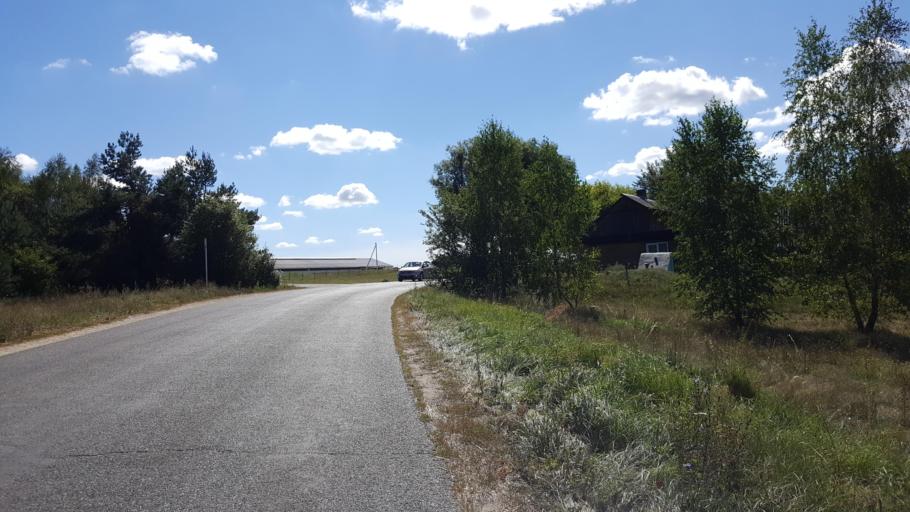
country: BY
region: Brest
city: Vysokaye
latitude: 52.3389
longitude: 23.3500
